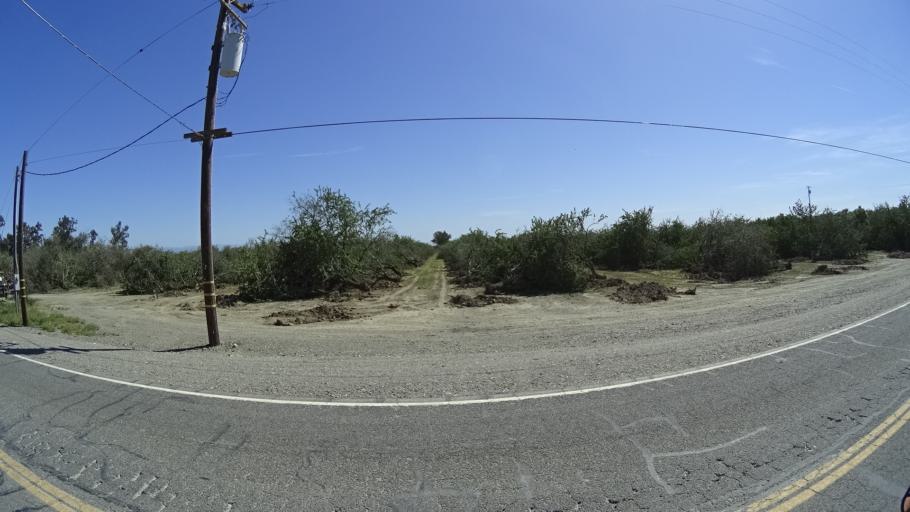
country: US
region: California
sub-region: Glenn County
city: Orland
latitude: 39.7201
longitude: -122.1410
